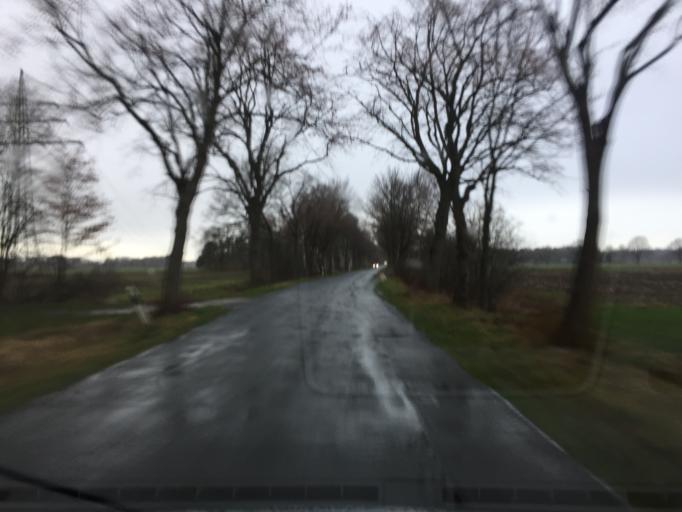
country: DE
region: Lower Saxony
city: Barenburg
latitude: 52.6488
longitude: 8.8203
